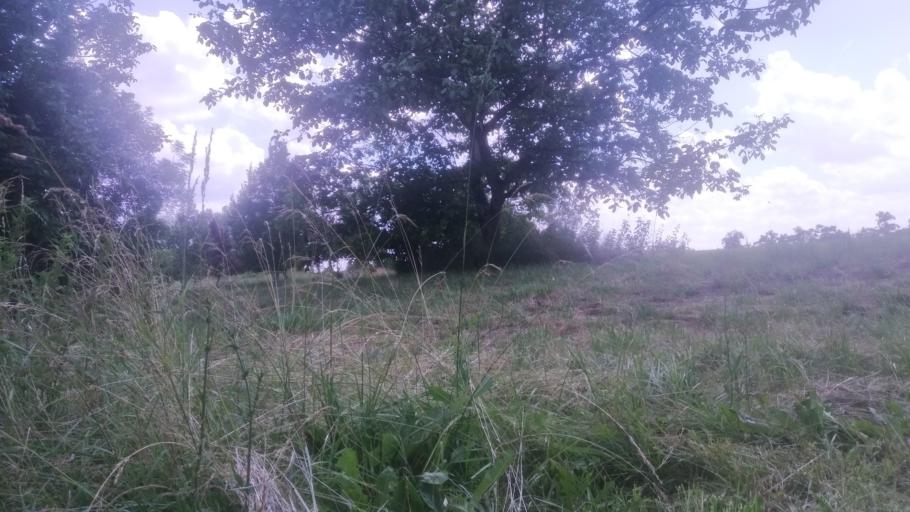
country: HU
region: Pest
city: Pilis
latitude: 47.2821
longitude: 19.5557
